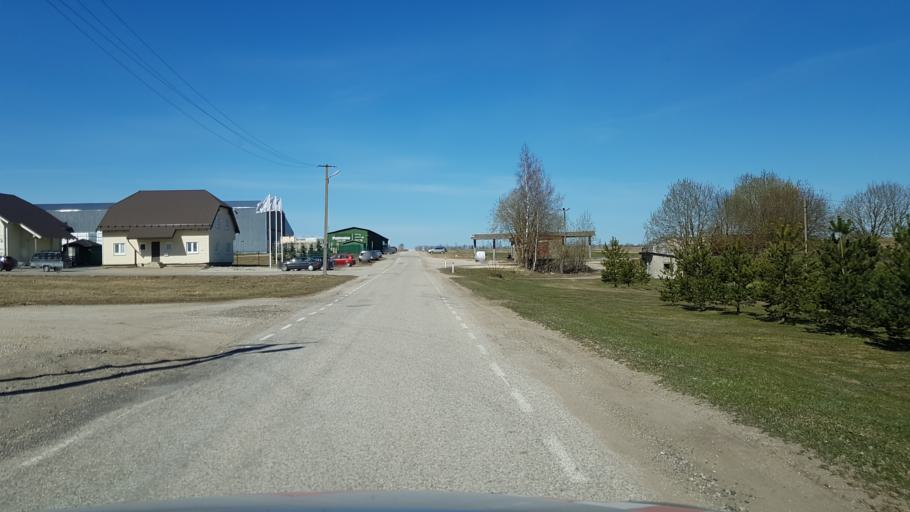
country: EE
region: Laeaene-Virumaa
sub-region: Vinni vald
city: Vinni
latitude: 59.0700
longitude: 26.5556
